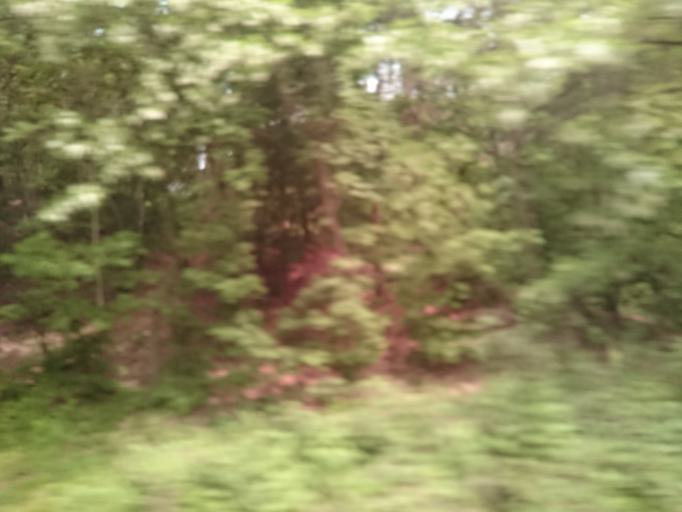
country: KR
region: Jeollabuk-do
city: Wanju
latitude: 35.9003
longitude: 127.1968
